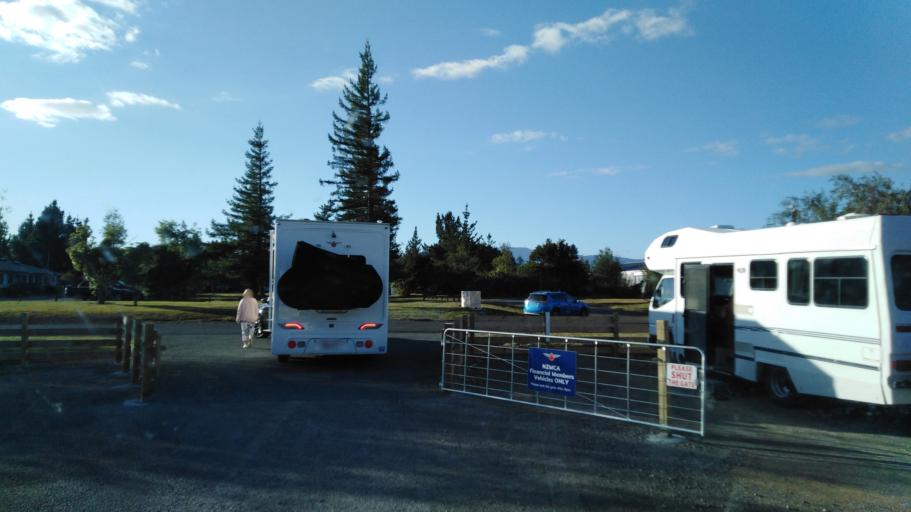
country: NZ
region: Waikato
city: Turangi
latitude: -38.9952
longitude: 175.7992
